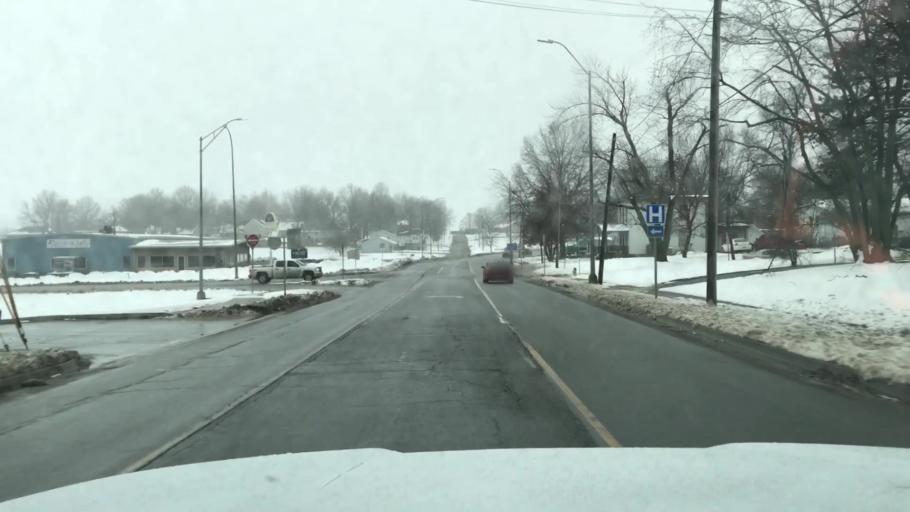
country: US
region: Missouri
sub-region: Clinton County
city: Cameron
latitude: 39.7324
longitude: -94.2360
